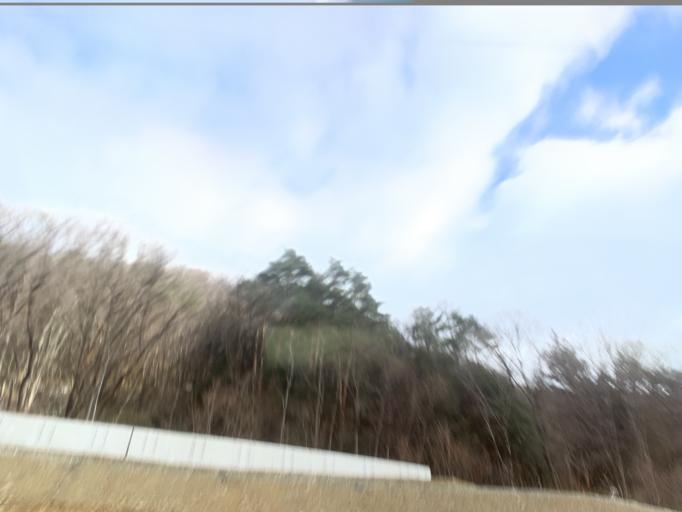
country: JP
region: Gifu
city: Takayama
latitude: 36.0184
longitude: 137.2901
